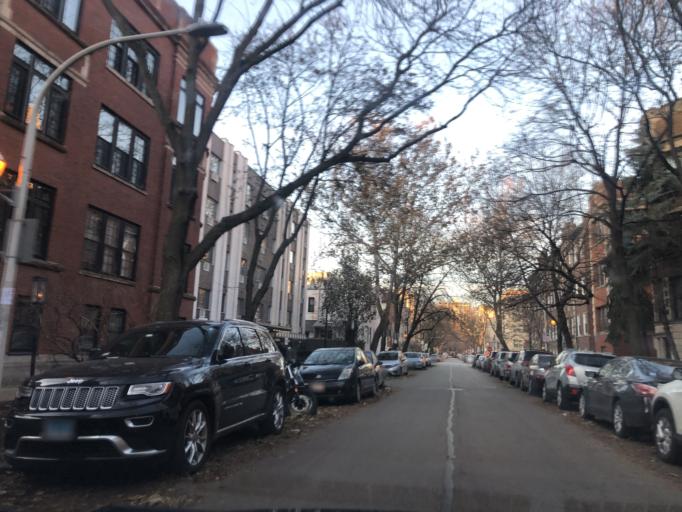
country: US
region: Illinois
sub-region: Cook County
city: Chicago
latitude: 41.9347
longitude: -87.6417
